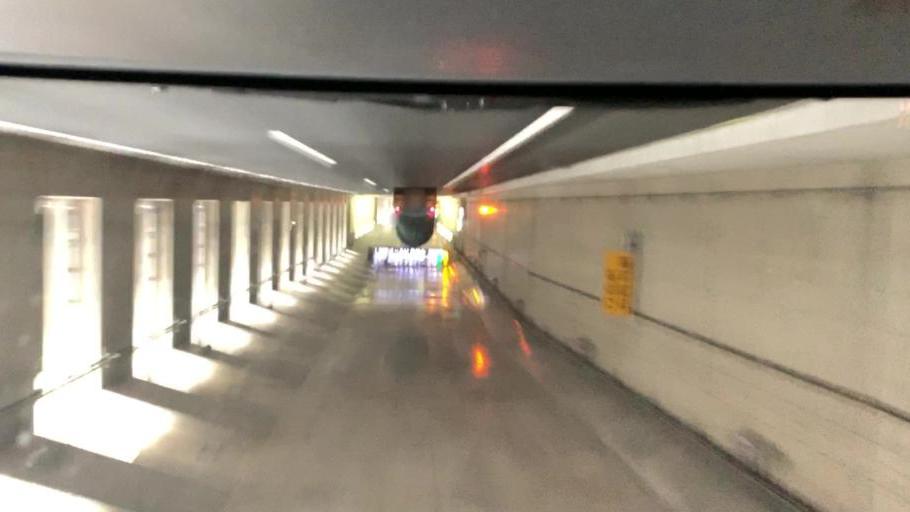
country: JP
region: Tokyo
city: Urayasu
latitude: 35.7139
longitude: 139.9210
